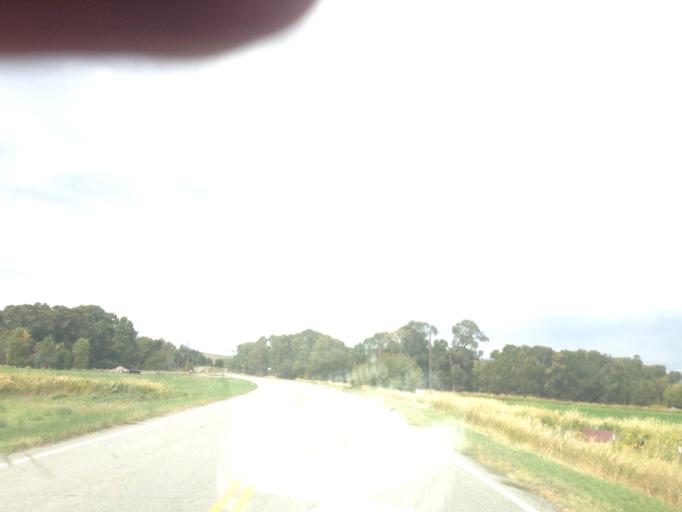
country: US
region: Montana
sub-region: Sweet Grass County
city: Big Timber
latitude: 45.7838
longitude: -109.8337
